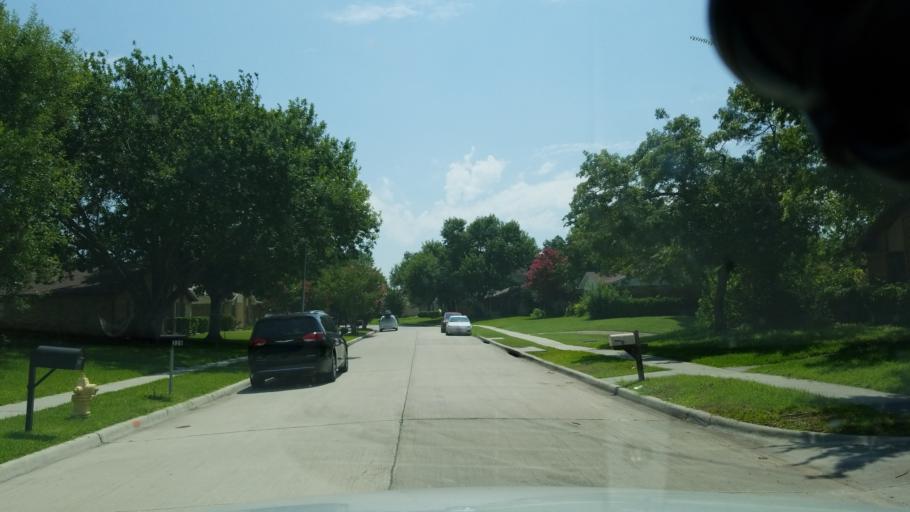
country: US
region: Texas
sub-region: Dallas County
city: Coppell
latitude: 32.9650
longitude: -96.9857
